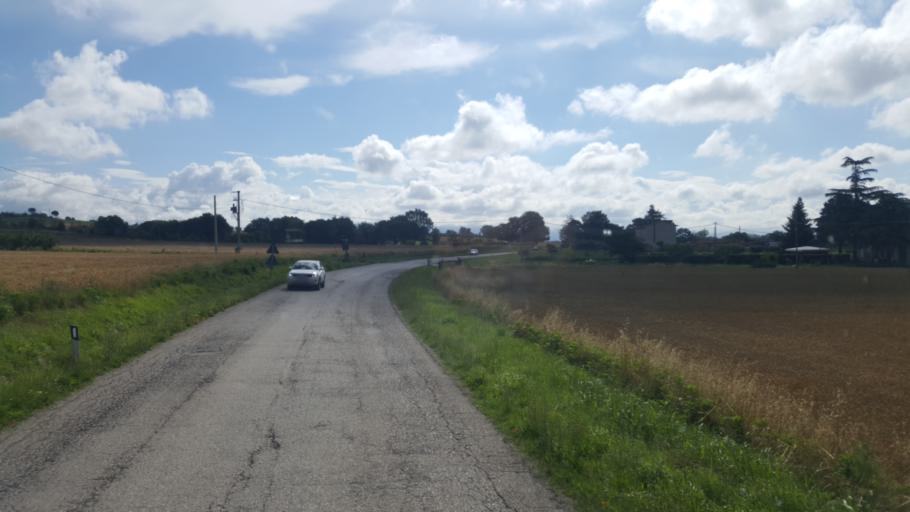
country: IT
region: Umbria
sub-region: Provincia di Perugia
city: Torgiano
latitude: 43.0374
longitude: 12.4577
